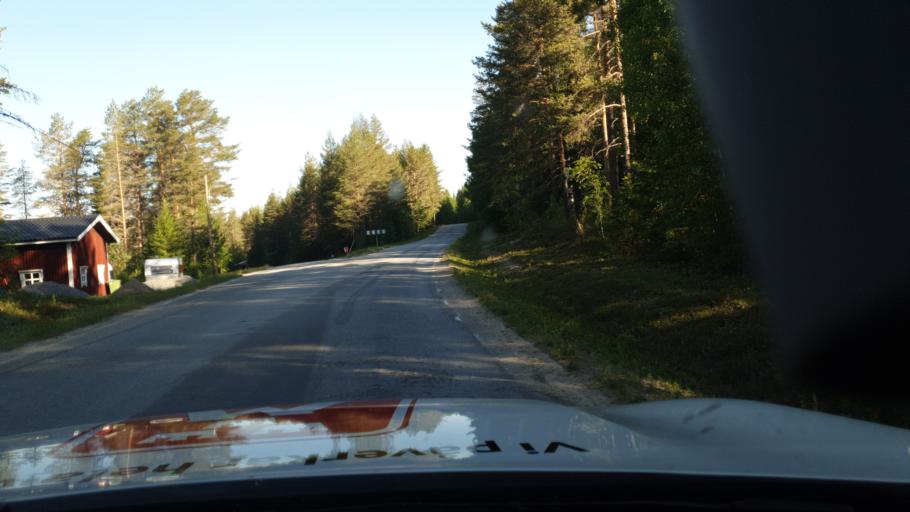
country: SE
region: Vaesterbotten
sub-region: Vannas Kommun
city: Vannasby
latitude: 64.0794
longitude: 20.0524
